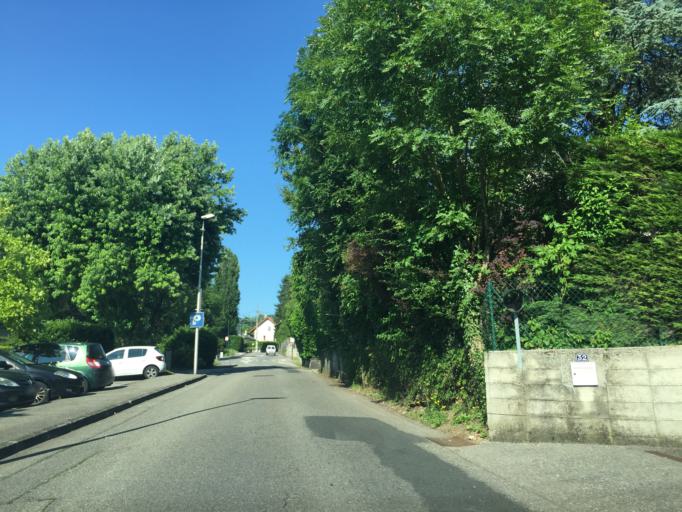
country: FR
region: Rhone-Alpes
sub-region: Departement de la Savoie
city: Aix-les-Bains
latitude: 45.6847
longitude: 5.9208
